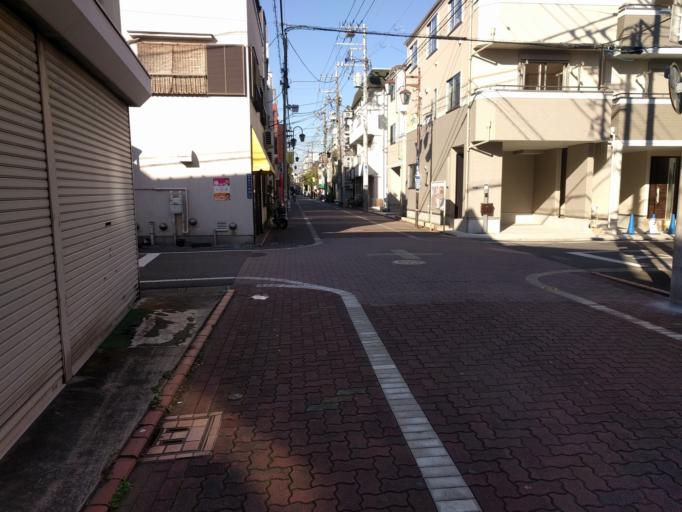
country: JP
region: Kanagawa
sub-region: Kawasaki-shi
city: Kawasaki
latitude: 35.5719
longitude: 139.7177
